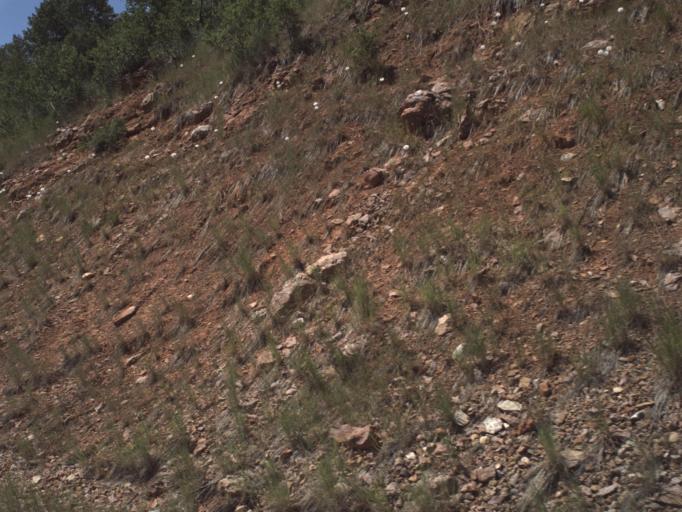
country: US
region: Utah
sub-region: Weber County
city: Wolf Creek
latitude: 41.4045
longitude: -111.5475
